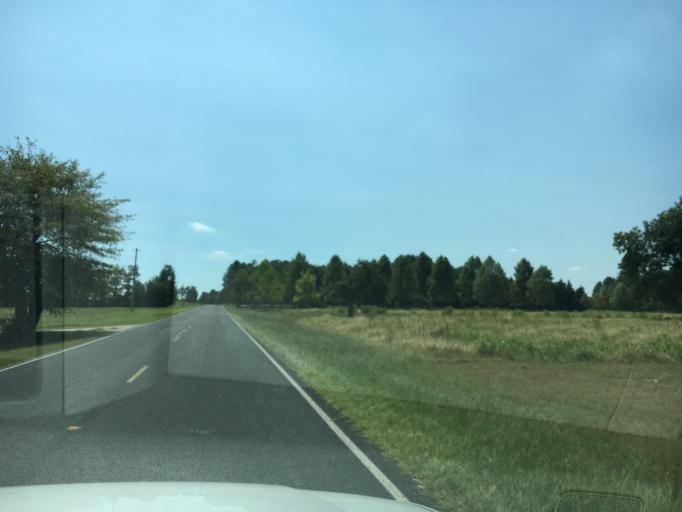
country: US
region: South Carolina
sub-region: Lexington County
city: Batesburg
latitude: 33.8079
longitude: -81.6475
